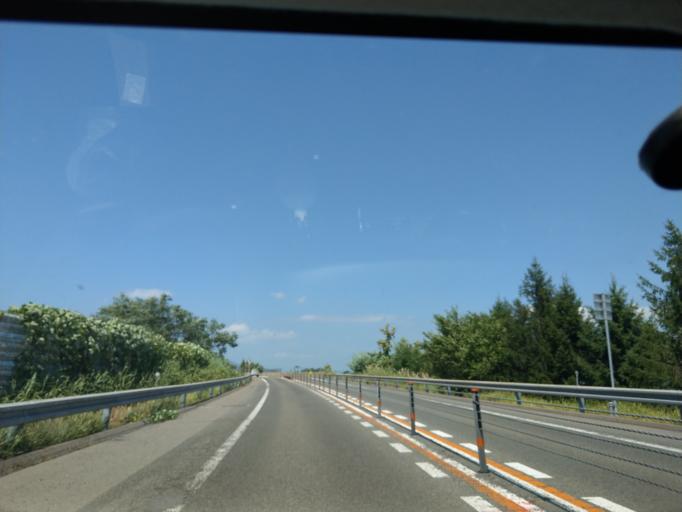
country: JP
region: Akita
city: Yokotemachi
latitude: 39.3519
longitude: 140.4967
